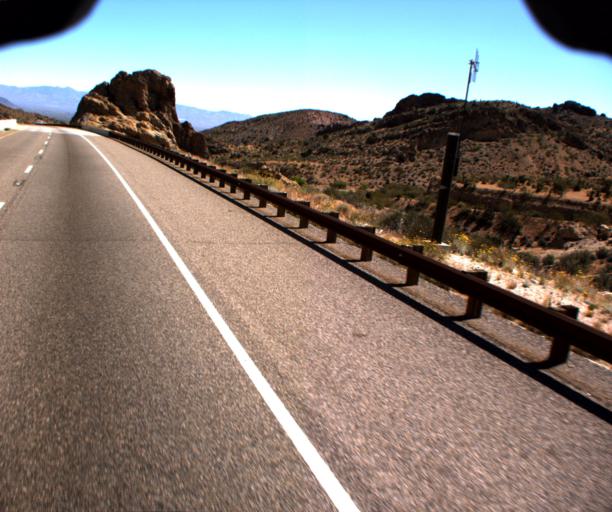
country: US
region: Arizona
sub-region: Mohave County
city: Golden Valley
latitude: 35.2194
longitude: -114.3903
